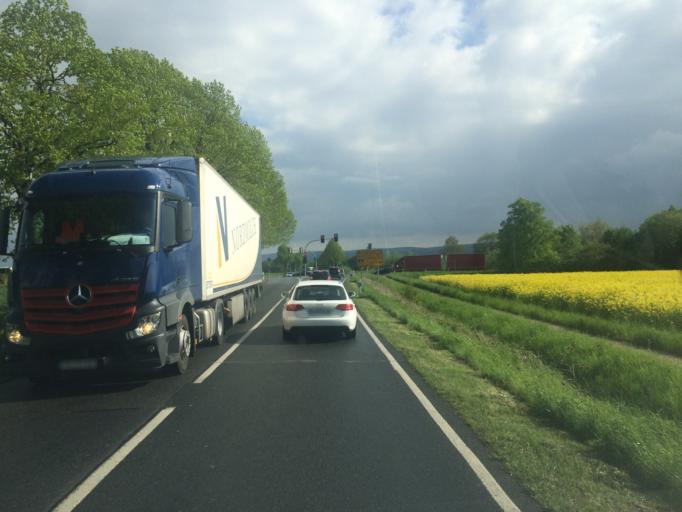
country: DE
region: Lower Saxony
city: Gross Munzel
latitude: 52.3339
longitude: 9.4667
